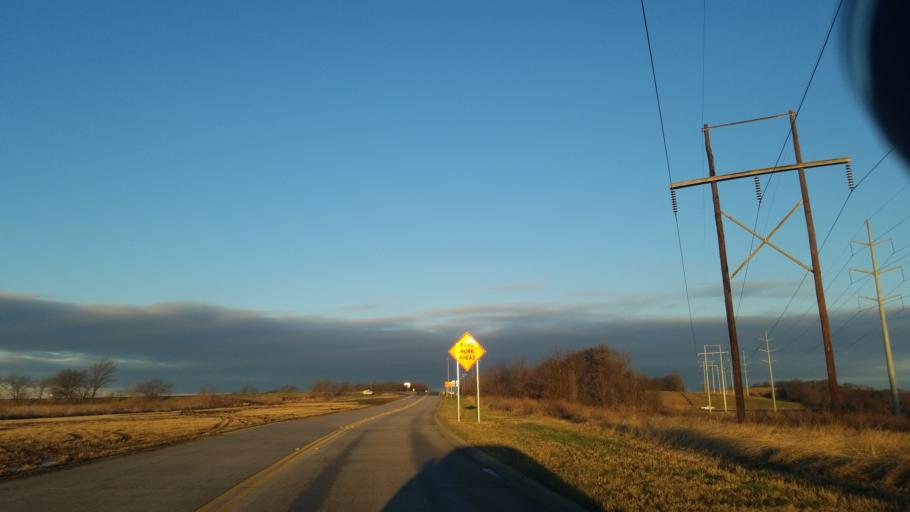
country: US
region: Texas
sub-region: Denton County
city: Argyle
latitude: 33.1705
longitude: -97.1781
